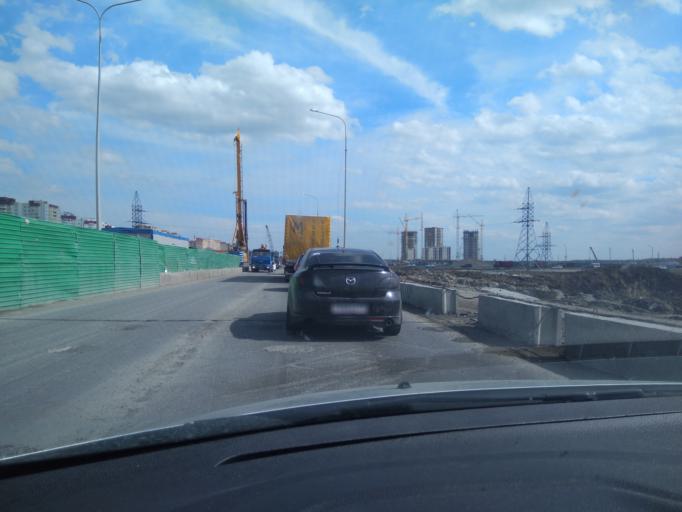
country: RU
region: Tjumen
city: Tyumen
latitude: 57.1060
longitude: 65.5587
